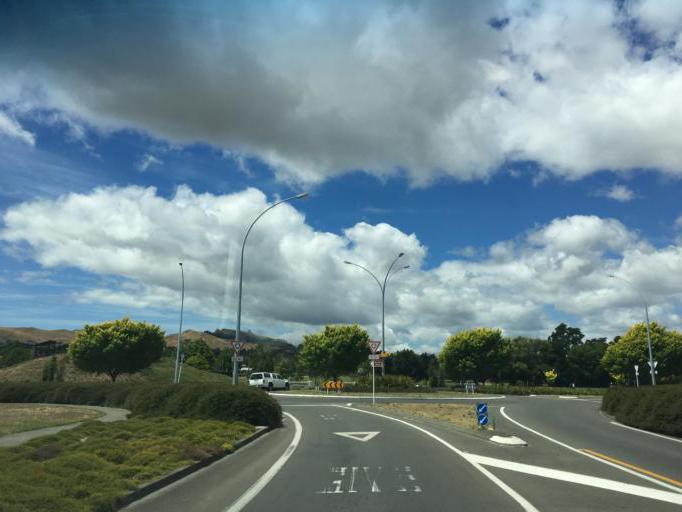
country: NZ
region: Hawke's Bay
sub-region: Hastings District
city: Hastings
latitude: -39.6587
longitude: 176.8860
